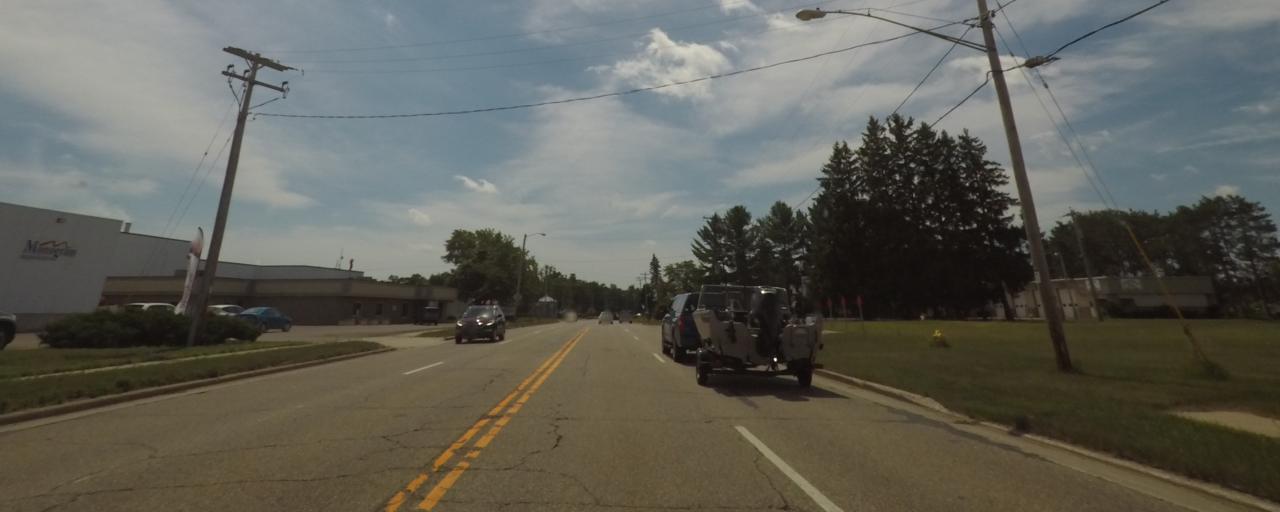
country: US
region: Wisconsin
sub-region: Portage County
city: Whiting
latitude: 44.4777
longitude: -89.5483
